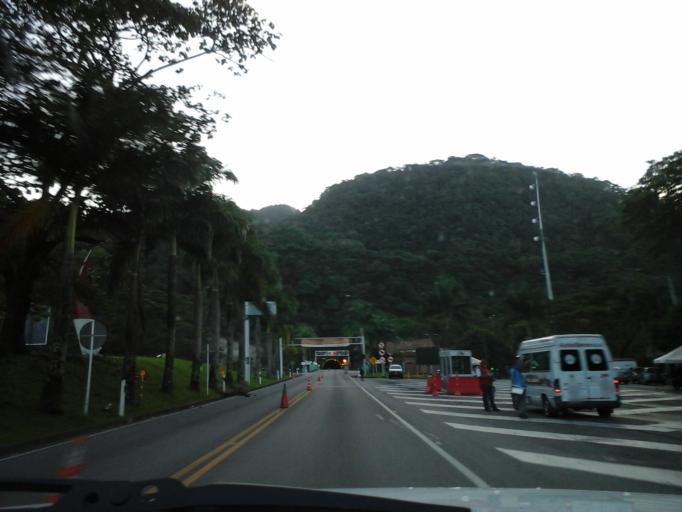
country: CO
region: Meta
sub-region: Villavicencio
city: Villavicencio
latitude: 4.1422
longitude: -73.6609
